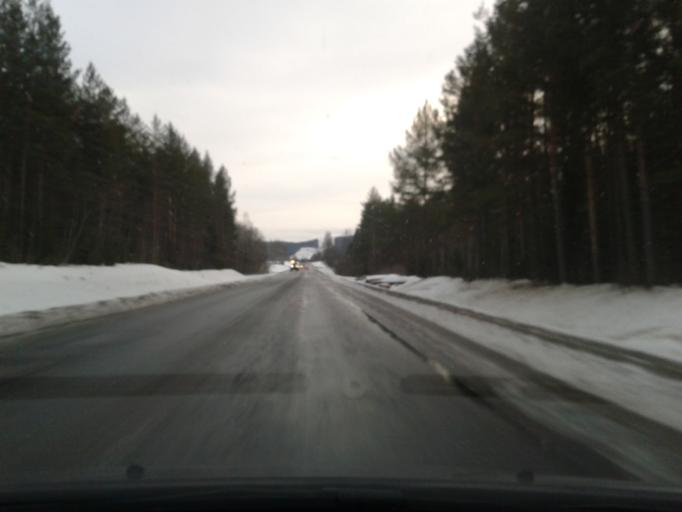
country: SE
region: Vaesternorrland
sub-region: Solleftea Kommun
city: Solleftea
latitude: 63.2541
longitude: 17.2168
